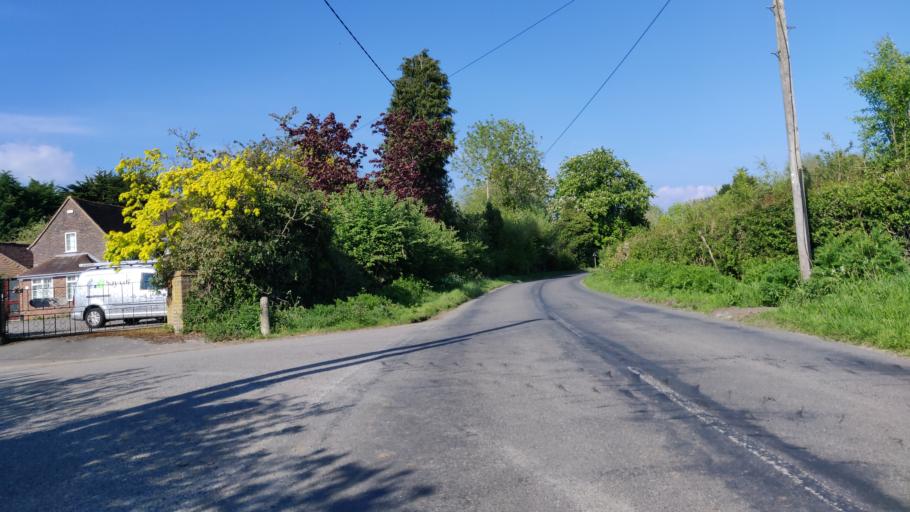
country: GB
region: England
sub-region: West Sussex
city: Southwater
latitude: 51.0323
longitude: -0.3687
